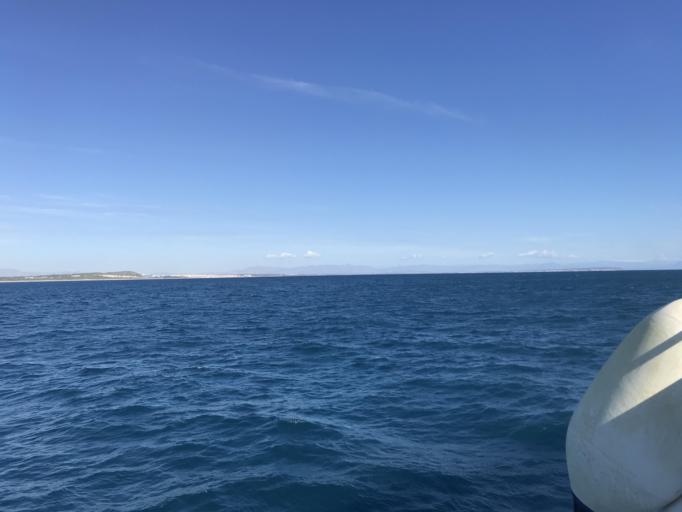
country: ES
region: Valencia
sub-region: Provincia de Alicante
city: Torrevieja
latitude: 38.0131
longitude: -0.6272
